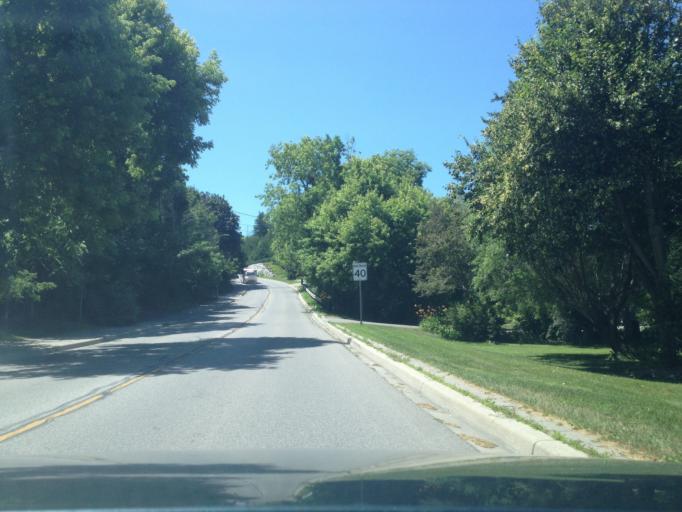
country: CA
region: Ontario
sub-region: Halton
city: Milton
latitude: 43.6655
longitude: -79.9276
